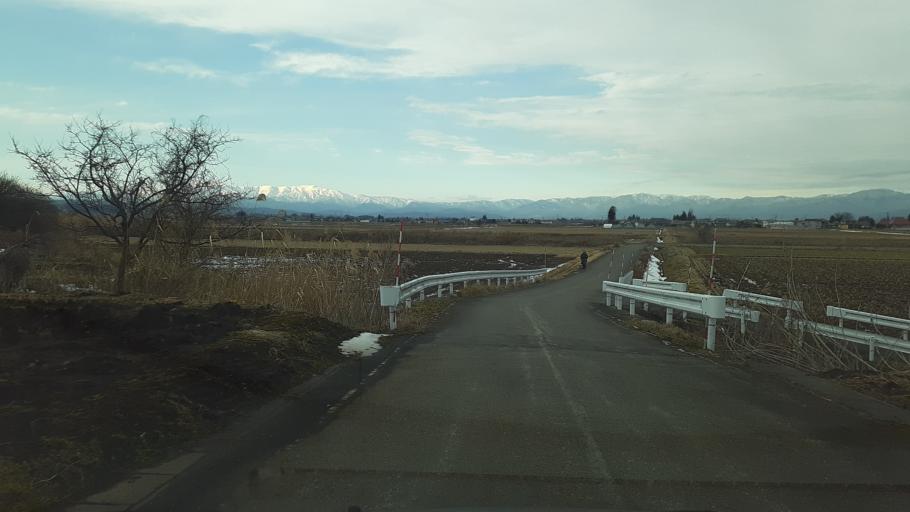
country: JP
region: Fukushima
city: Kitakata
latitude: 37.4713
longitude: 139.8473
